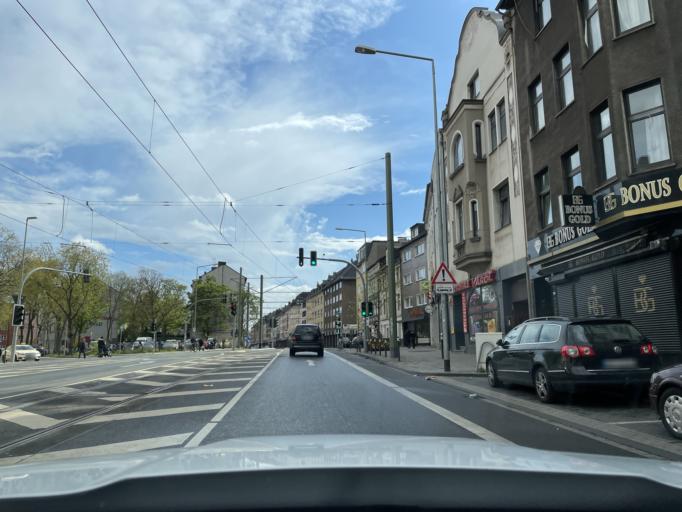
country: DE
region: North Rhine-Westphalia
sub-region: Regierungsbezirk Dusseldorf
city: Hochfeld
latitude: 51.4232
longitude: 6.7546
